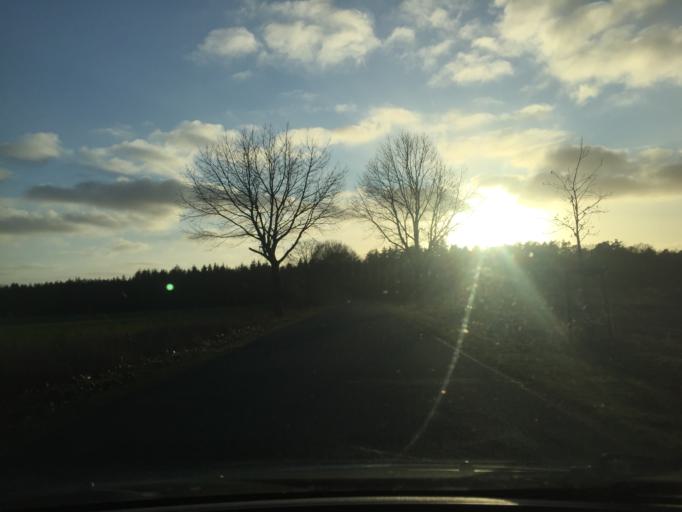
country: DE
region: Lower Saxony
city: Hitzacker
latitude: 53.1723
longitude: 10.9741
